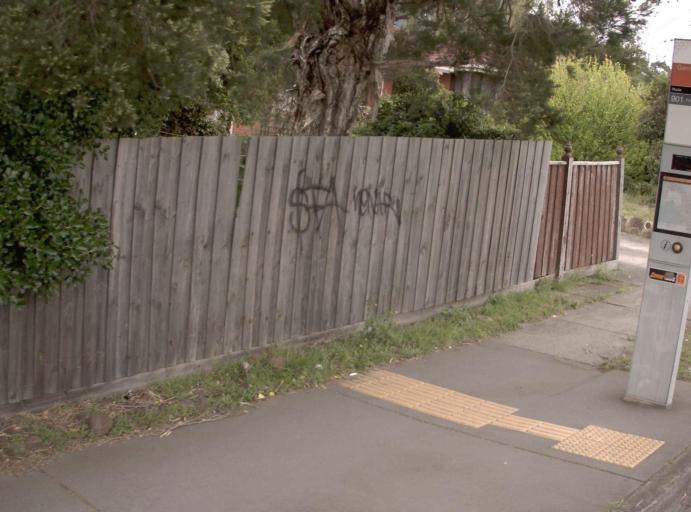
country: AU
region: Victoria
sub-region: Knox
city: Wantirna
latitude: -37.8467
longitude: 145.2273
